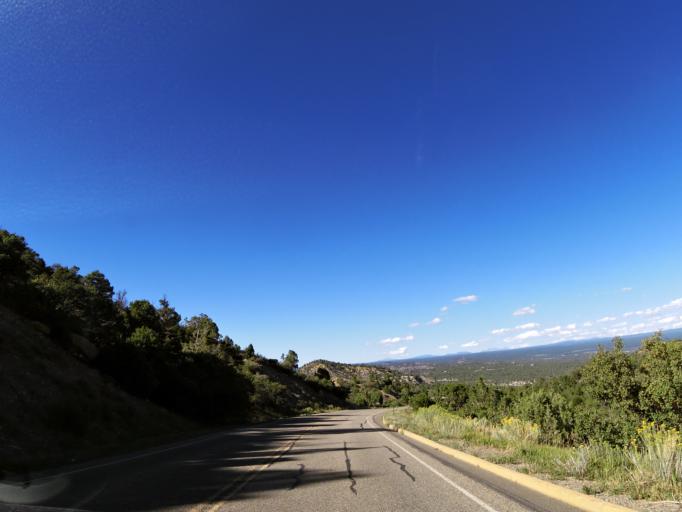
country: US
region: Colorado
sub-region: Montezuma County
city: Mancos
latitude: 37.3223
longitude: -108.4182
